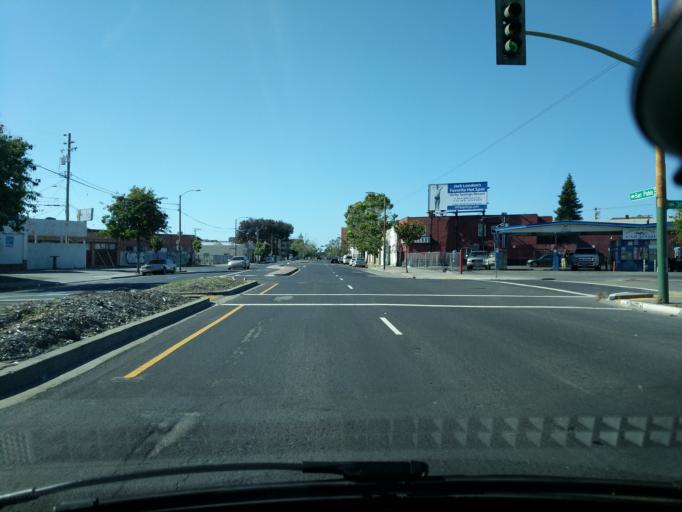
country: US
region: California
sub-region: Alameda County
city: Emeryville
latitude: 37.8212
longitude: -122.2767
